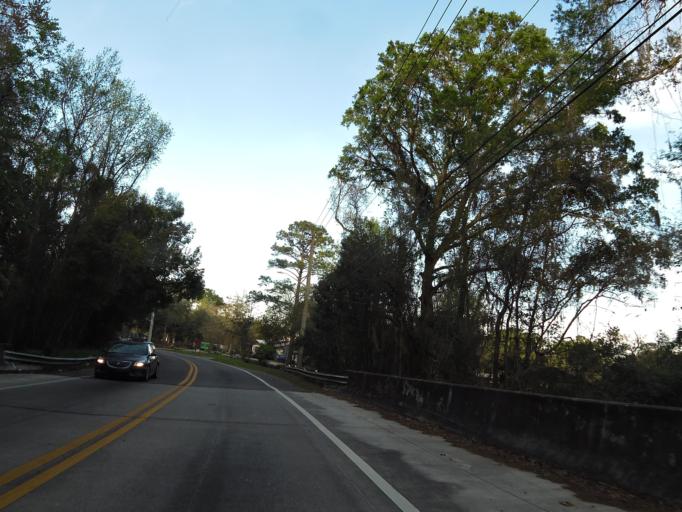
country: US
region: Florida
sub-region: Duval County
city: Jacksonville
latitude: 30.4683
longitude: -81.6565
